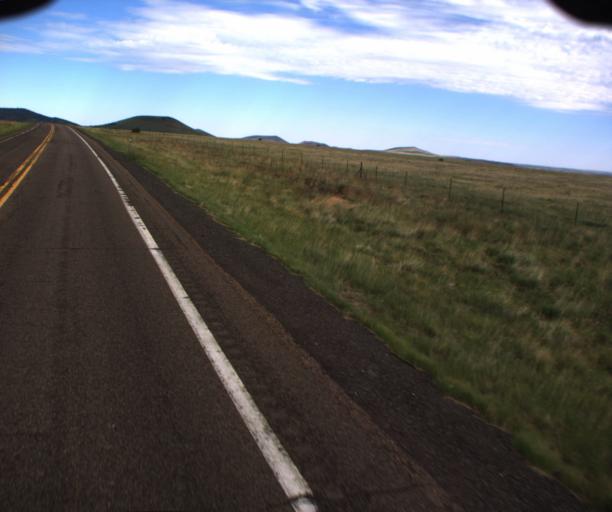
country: US
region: Arizona
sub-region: Apache County
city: Springerville
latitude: 34.2351
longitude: -109.5002
